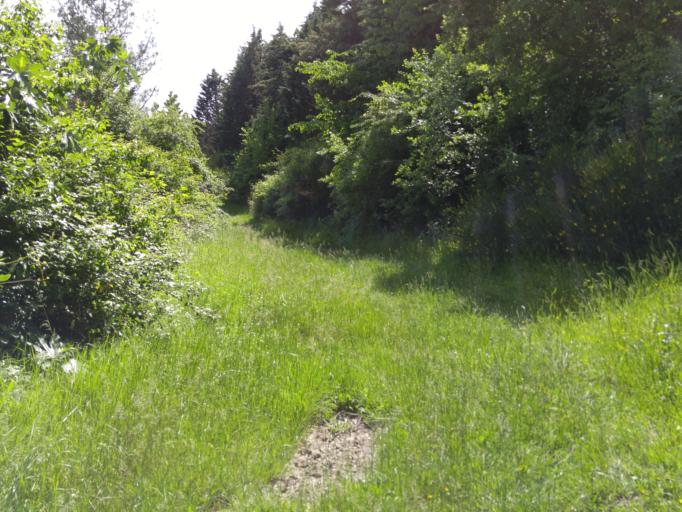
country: IT
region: The Marches
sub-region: Provincia di Pesaro e Urbino
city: Fermignano
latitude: 43.7005
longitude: 12.6312
